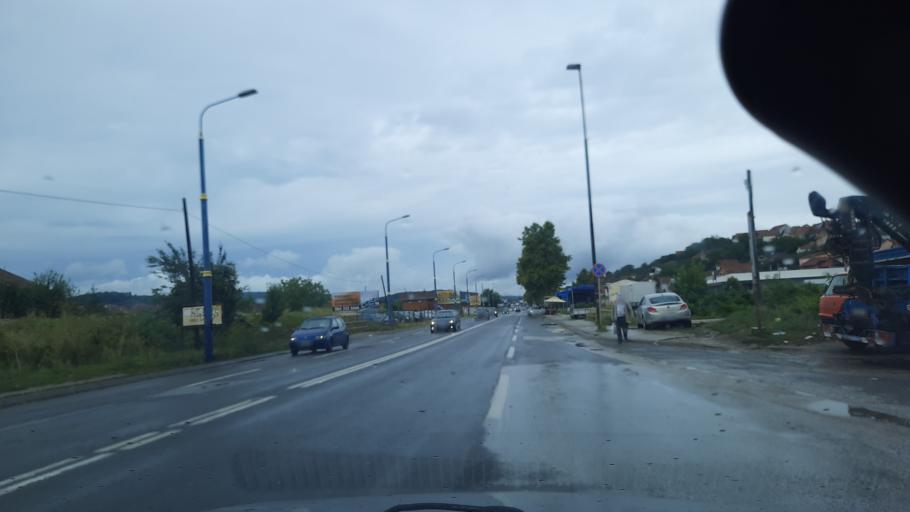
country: RS
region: Central Serbia
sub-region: Sumadijski Okrug
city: Kragujevac
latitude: 43.9980
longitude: 20.8833
